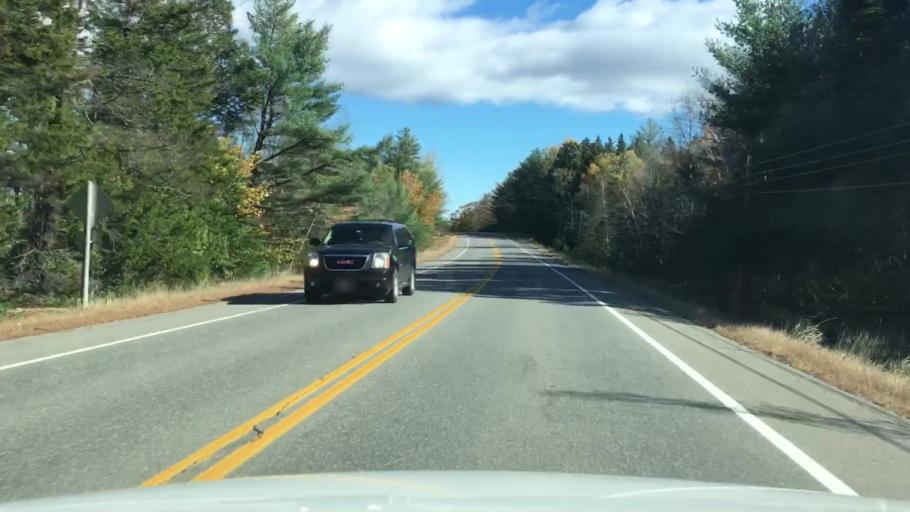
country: US
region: Maine
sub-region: Penobscot County
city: Millinocket
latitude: 45.6571
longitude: -68.6537
